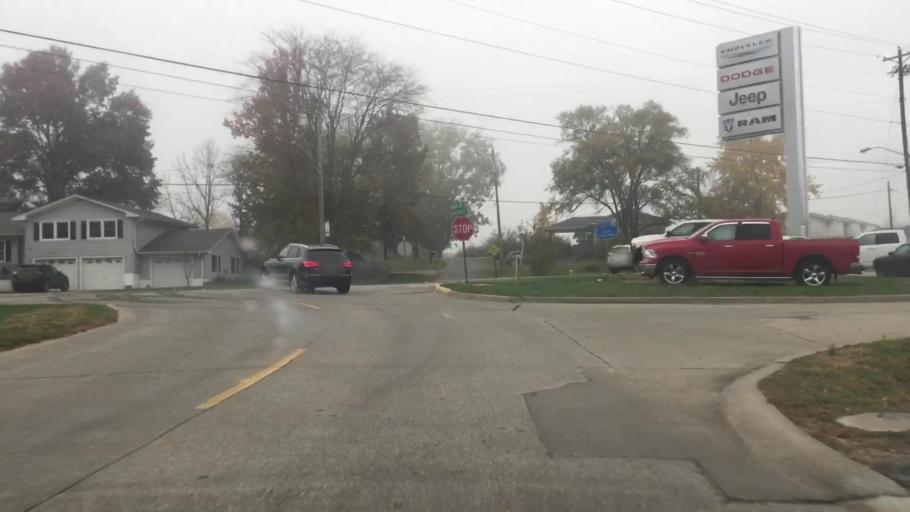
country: US
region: Missouri
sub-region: Callaway County
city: Fulton
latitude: 38.8367
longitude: -91.9546
